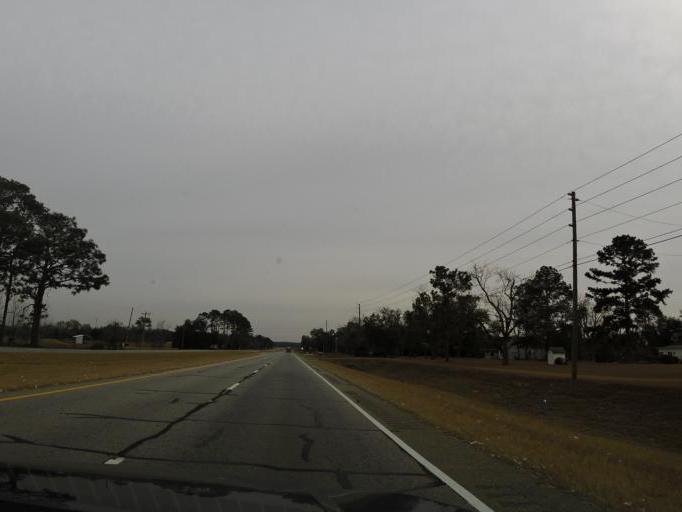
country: US
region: Georgia
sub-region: Decatur County
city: Bainbridge
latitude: 30.9542
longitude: -84.7097
